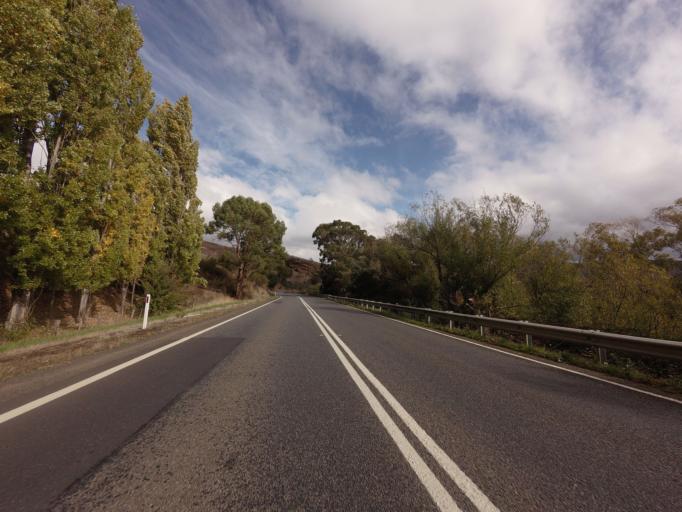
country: AU
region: Tasmania
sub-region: Derwent Valley
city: New Norfolk
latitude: -42.7310
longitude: 146.9567
